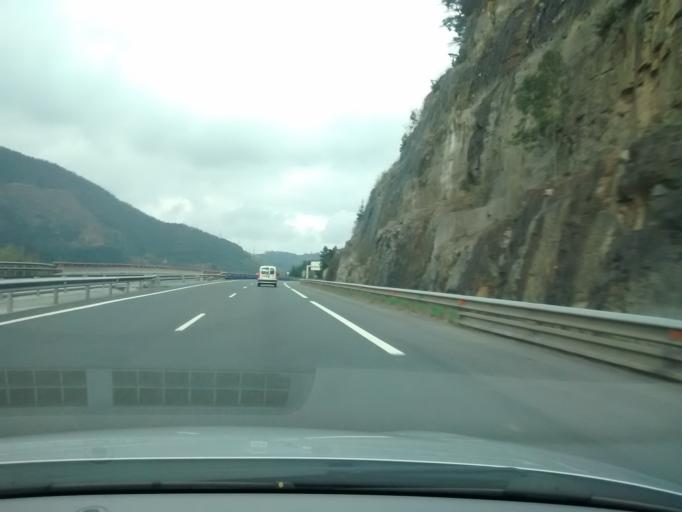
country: ES
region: Basque Country
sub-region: Bizkaia
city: Alonsotegi
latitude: 43.2385
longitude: -2.9991
